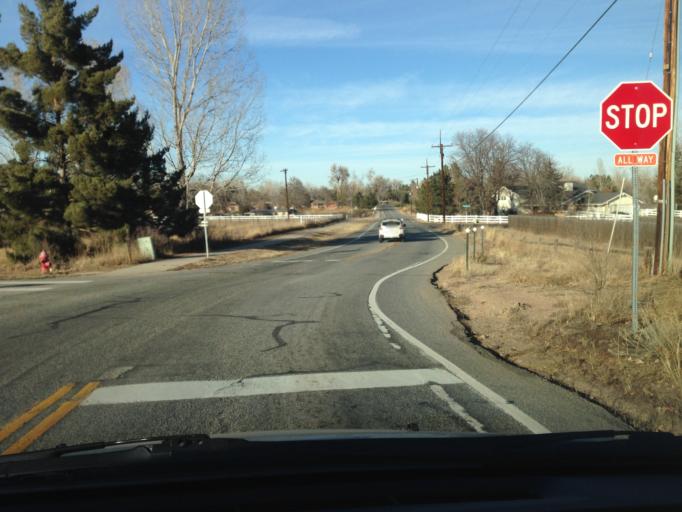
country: US
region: Colorado
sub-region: Boulder County
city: Niwot
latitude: 40.0941
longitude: -105.1690
